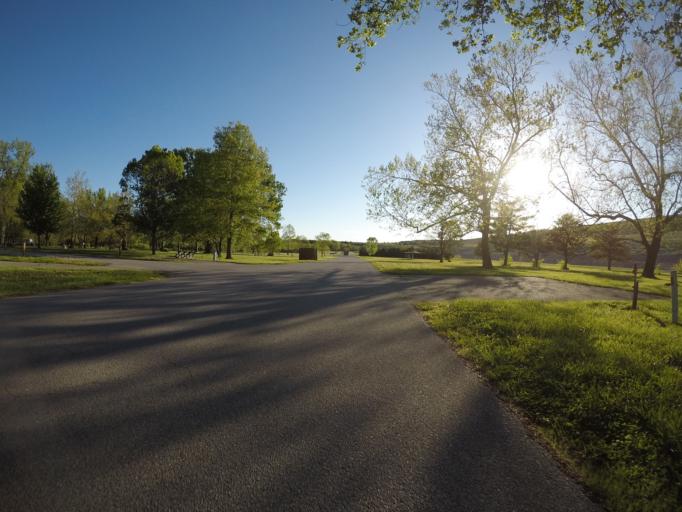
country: US
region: Kansas
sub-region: Riley County
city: Manhattan
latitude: 39.2546
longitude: -96.5916
